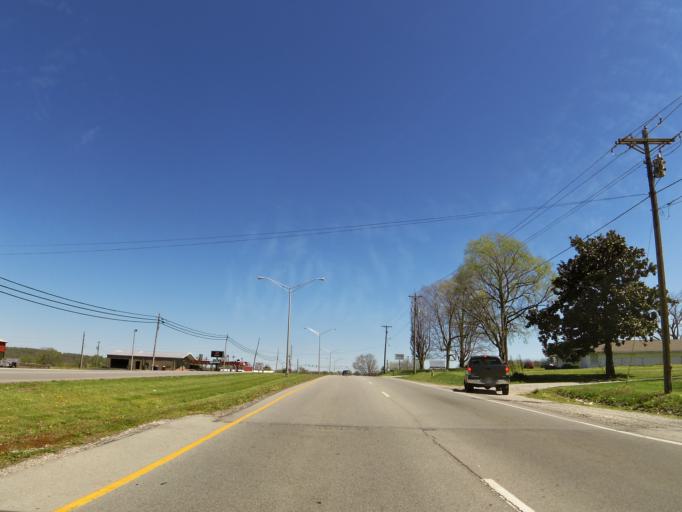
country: US
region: Kentucky
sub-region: Warren County
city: Bowling Green
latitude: 37.0093
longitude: -86.4027
